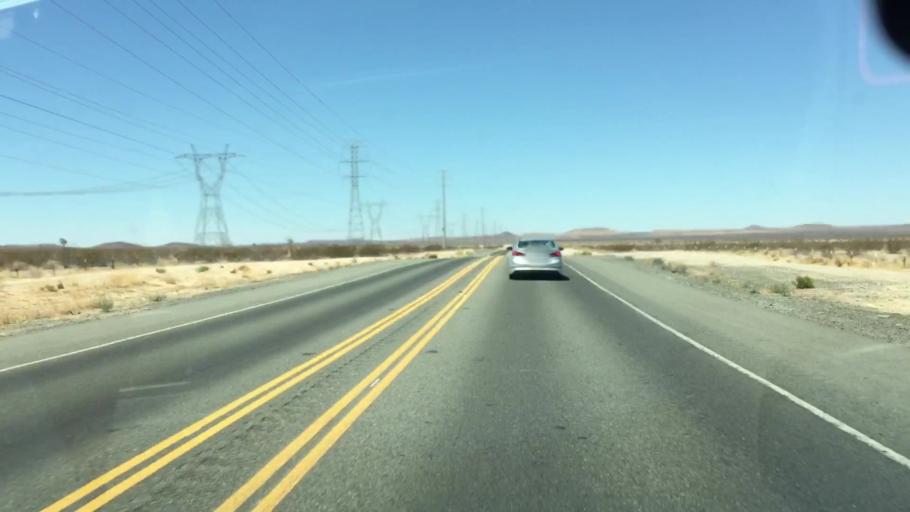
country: US
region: California
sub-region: San Bernardino County
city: Adelanto
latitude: 34.7825
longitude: -117.4814
